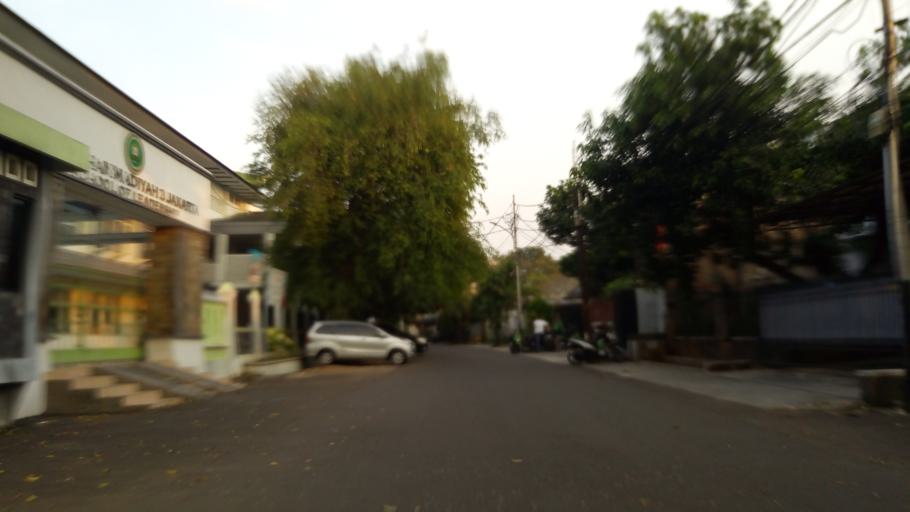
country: ID
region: Jakarta Raya
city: Jakarta
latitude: -6.2479
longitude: 106.7907
